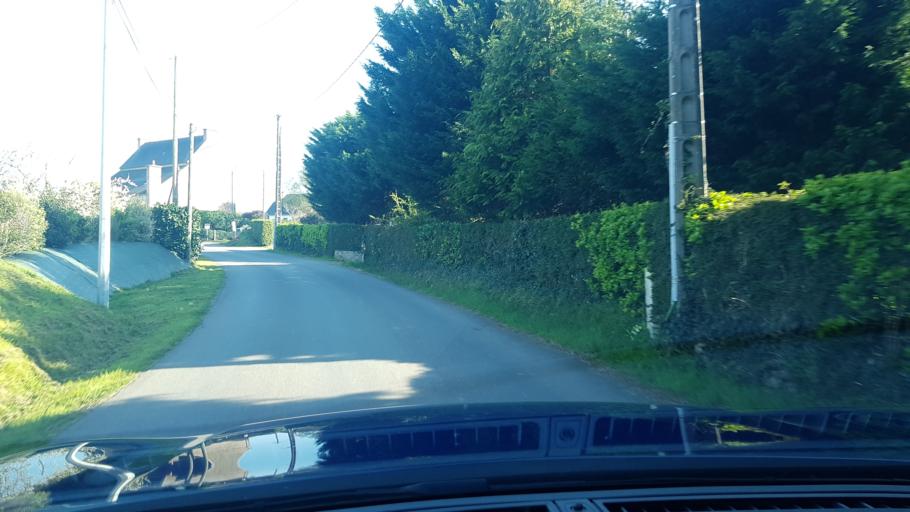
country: FR
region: Brittany
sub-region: Departement du Finistere
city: Clohars-Carnoet
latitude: 47.7783
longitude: -3.6173
